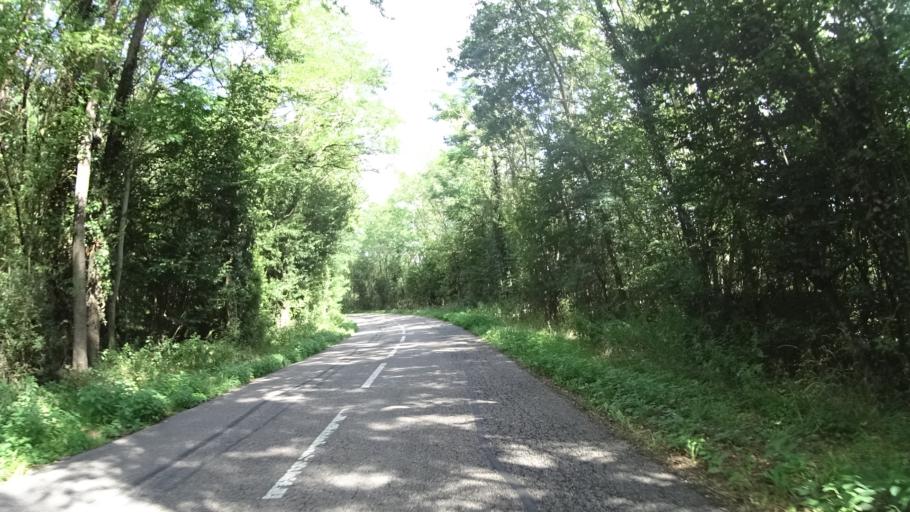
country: FR
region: Lorraine
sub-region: Departement de Meurthe-et-Moselle
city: Dommartin-les-Toul
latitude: 48.6472
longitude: 5.9168
